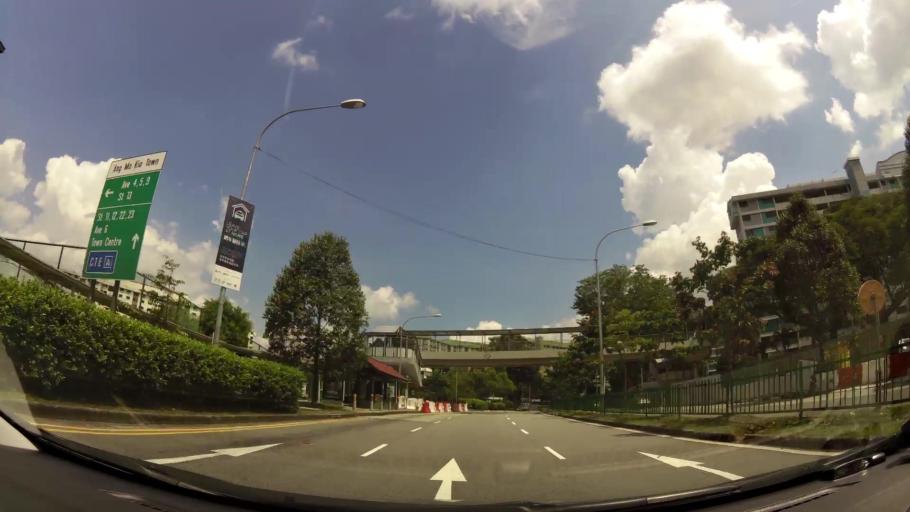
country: SG
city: Singapore
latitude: 1.3684
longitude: 103.8363
